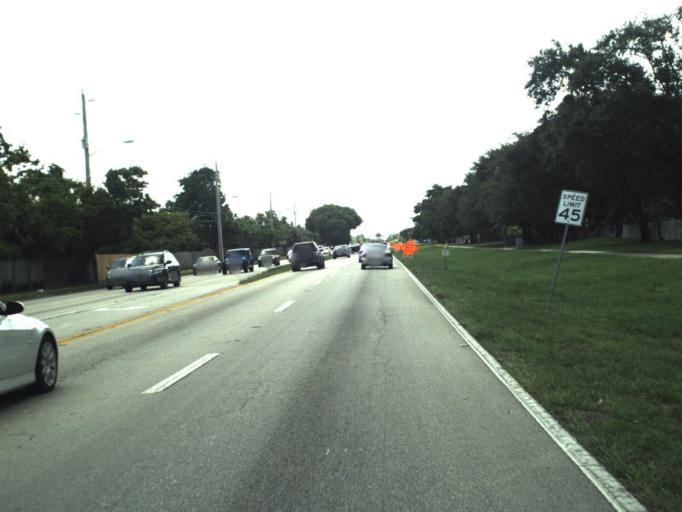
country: US
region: Florida
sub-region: Broward County
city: Miramar
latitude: 25.9944
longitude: -80.2574
